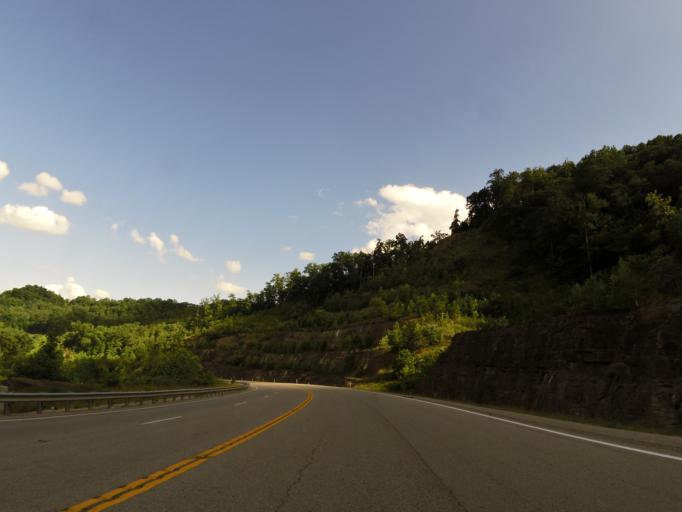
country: US
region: Kentucky
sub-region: Harlan County
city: Harlan
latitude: 36.7947
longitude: -83.2678
